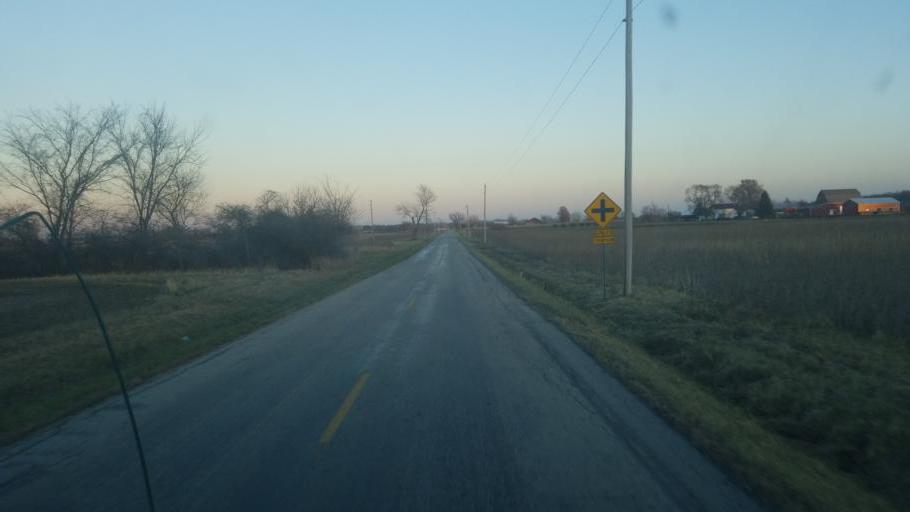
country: US
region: Ohio
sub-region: Marion County
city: Marion
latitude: 40.6223
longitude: -83.2718
